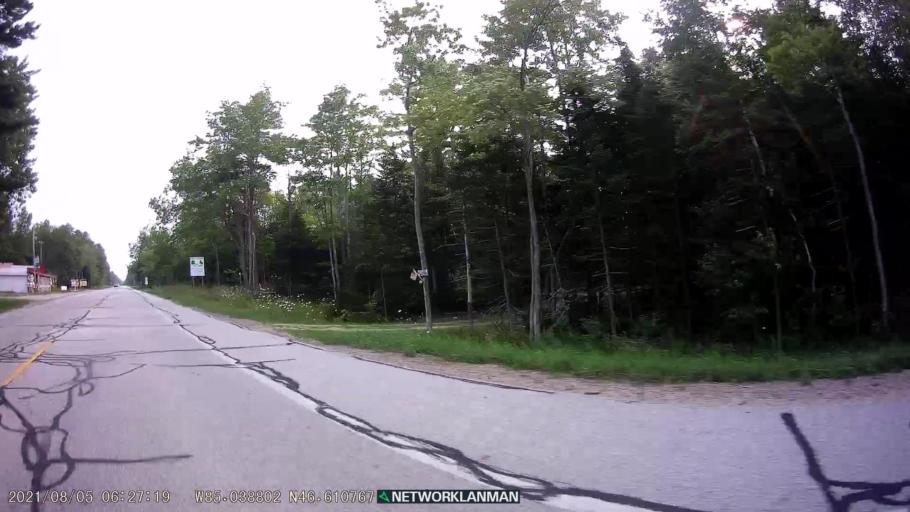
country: US
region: Michigan
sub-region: Luce County
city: Newberry
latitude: 46.6113
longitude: -85.0388
